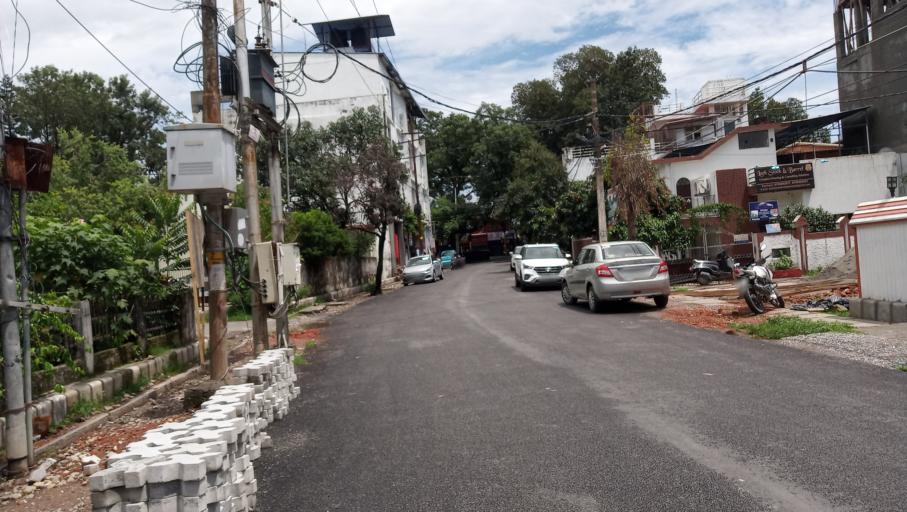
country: IN
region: Uttarakhand
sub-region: Dehradun
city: Dehradun
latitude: 30.3645
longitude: 78.0684
